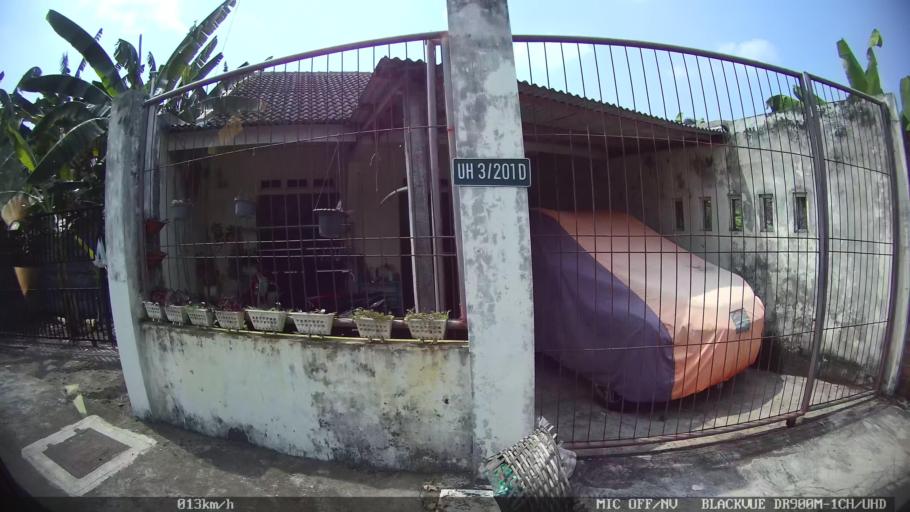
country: ID
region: Daerah Istimewa Yogyakarta
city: Yogyakarta
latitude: -7.8040
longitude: 110.3855
